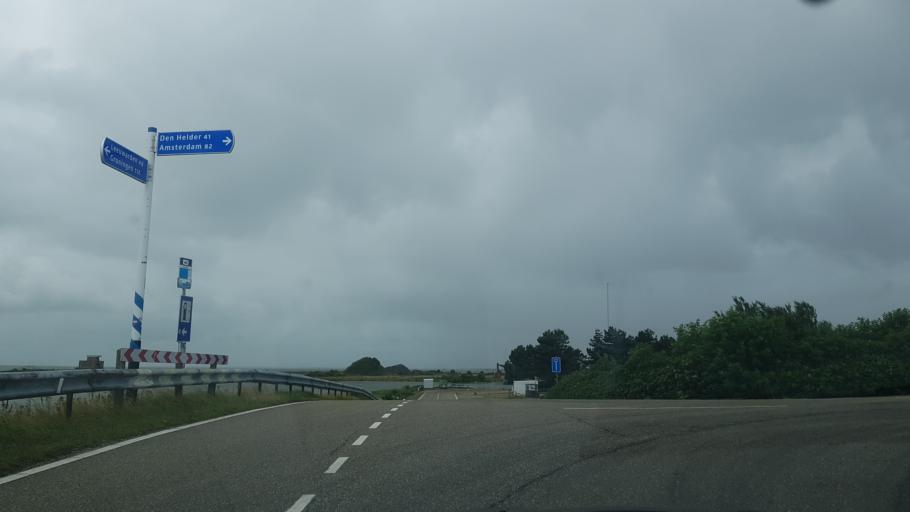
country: NL
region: Friesland
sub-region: Sudwest Fryslan
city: Makkum
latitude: 53.0199
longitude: 5.2096
